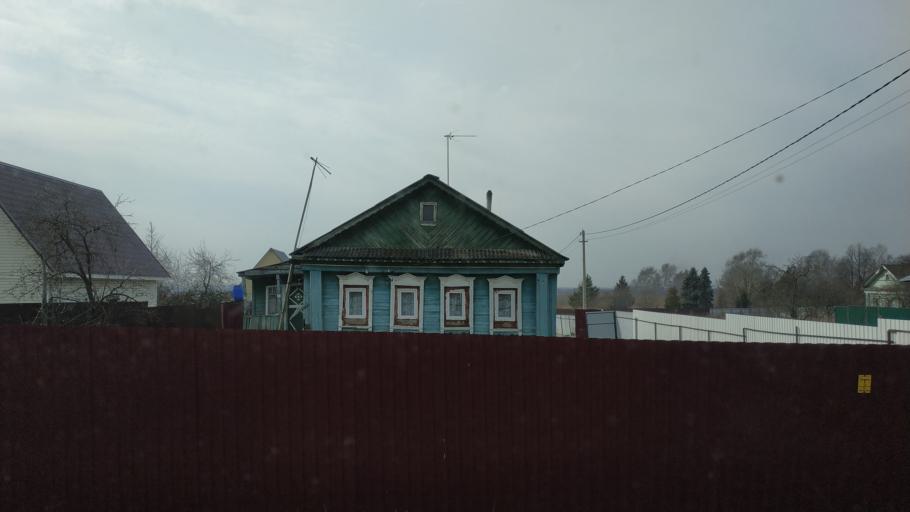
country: RU
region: Moskovskaya
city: Ashitkovo
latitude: 55.4214
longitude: 38.5499
